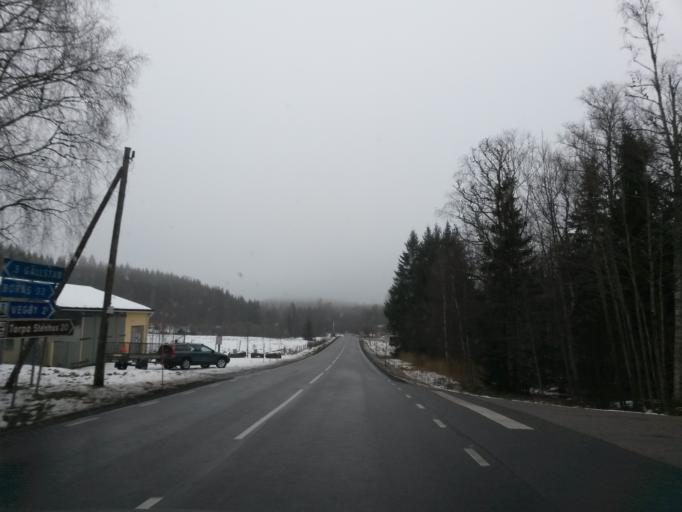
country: SE
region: Vaestra Goetaland
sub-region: Ulricehamns Kommun
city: Ulricehamn
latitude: 57.6745
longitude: 13.4015
